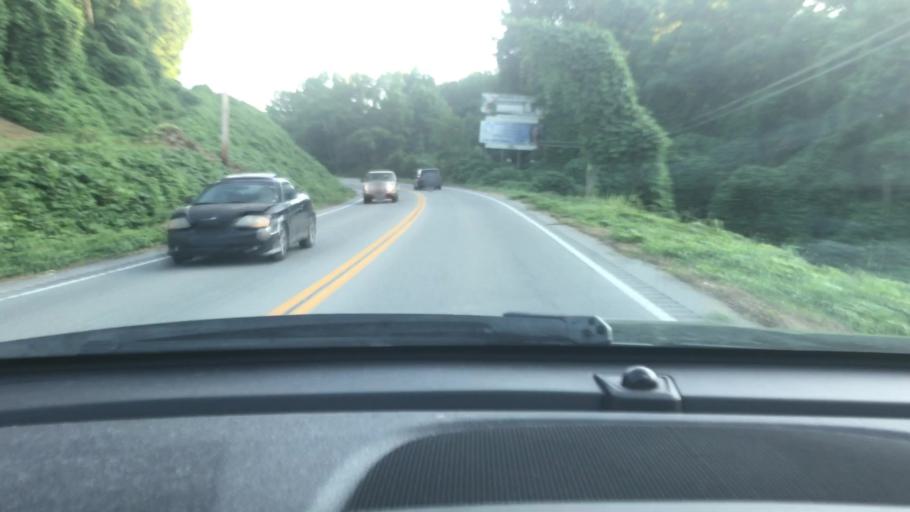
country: US
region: Tennessee
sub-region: Dickson County
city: Dickson
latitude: 36.1143
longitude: -87.3688
